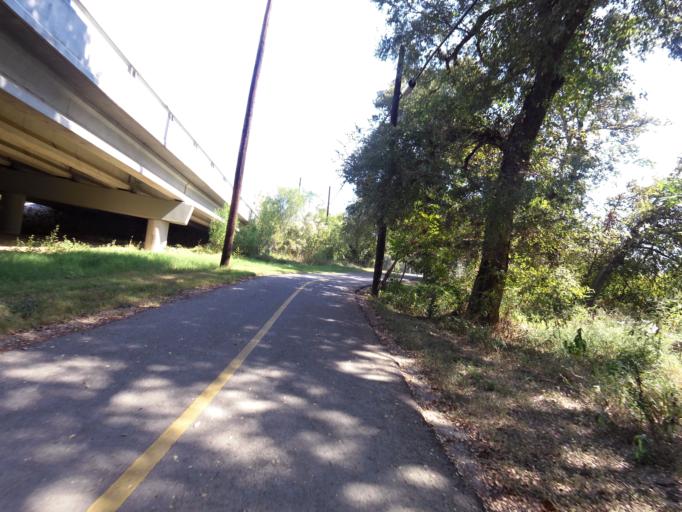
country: US
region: Texas
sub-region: Bexar County
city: San Antonio
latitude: 29.3985
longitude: -98.4264
